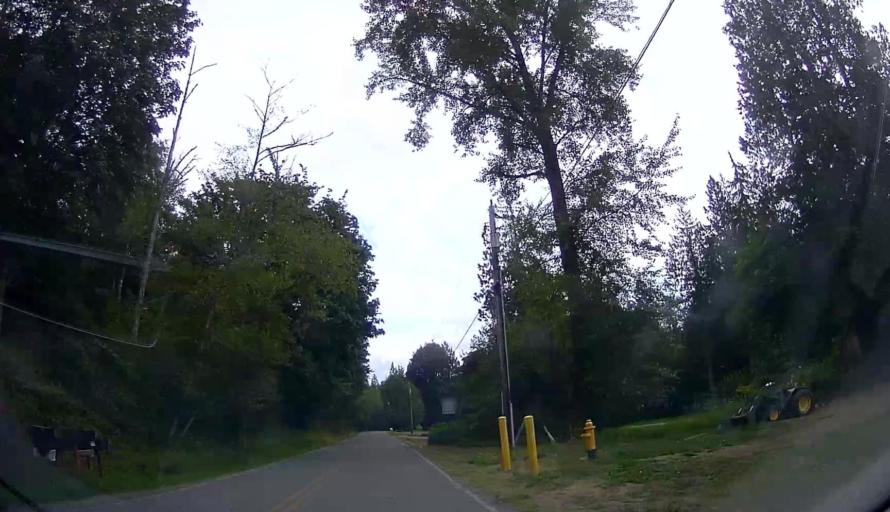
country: US
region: Washington
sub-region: Skagit County
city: Burlington
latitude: 48.5884
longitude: -122.3969
